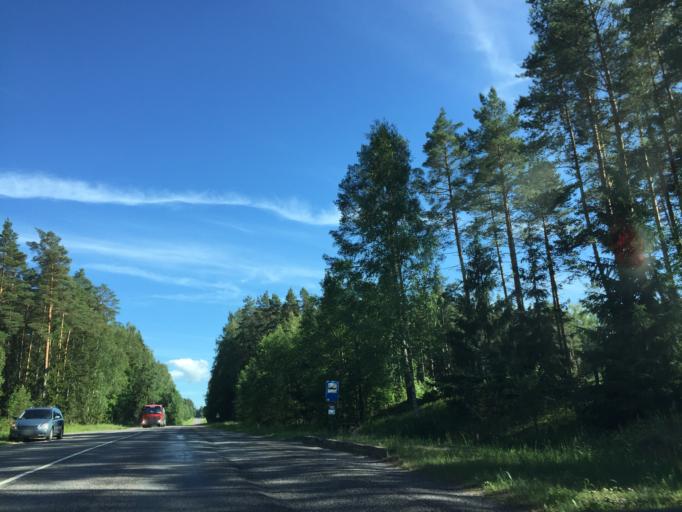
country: LV
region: Kuldigas Rajons
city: Kuldiga
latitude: 57.0623
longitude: 21.8127
